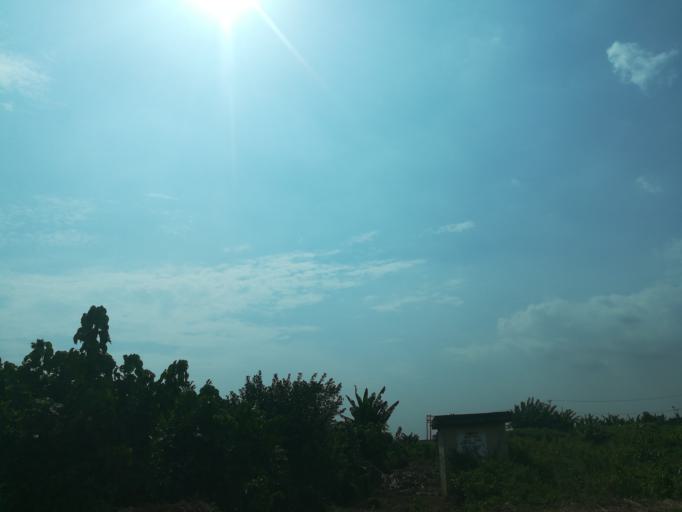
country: NG
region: Lagos
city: Ikorodu
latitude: 6.6389
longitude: 3.6700
